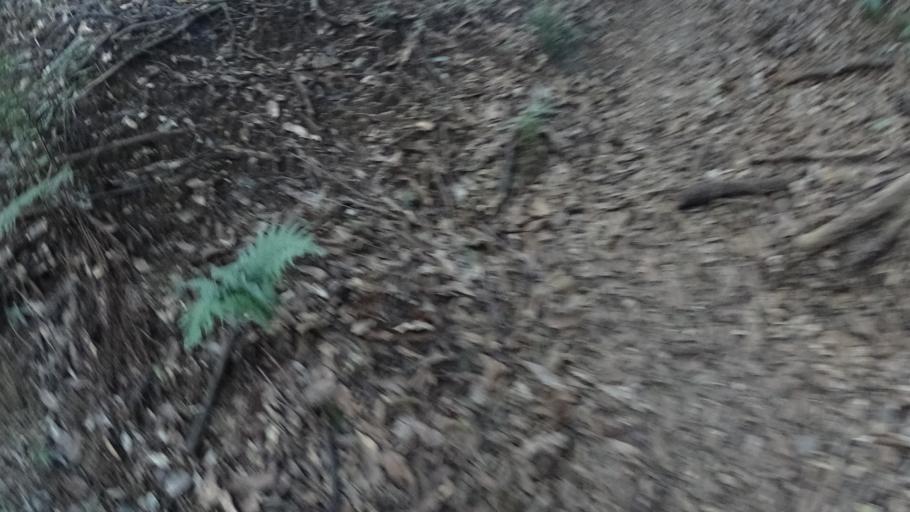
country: JP
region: Kanagawa
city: Hayama
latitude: 35.2845
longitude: 139.5934
